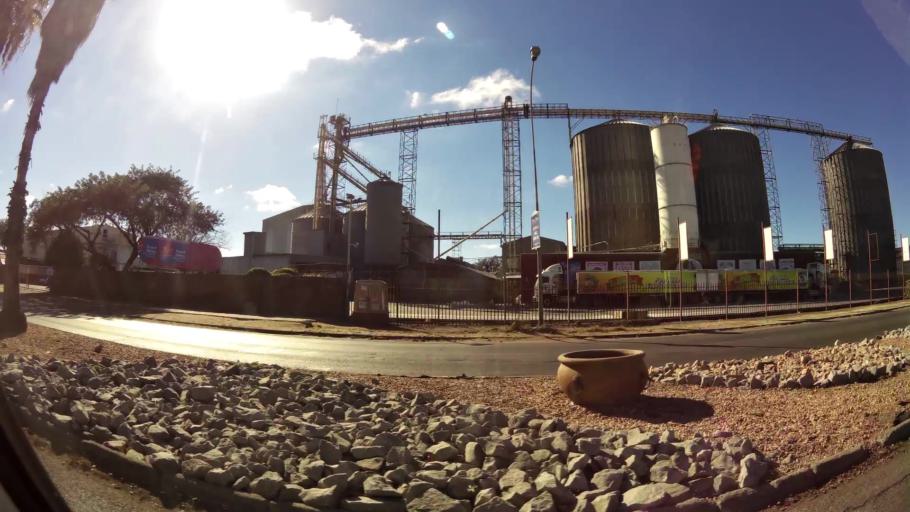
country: ZA
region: Limpopo
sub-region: Capricorn District Municipality
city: Polokwane
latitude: -23.8937
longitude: 29.4480
